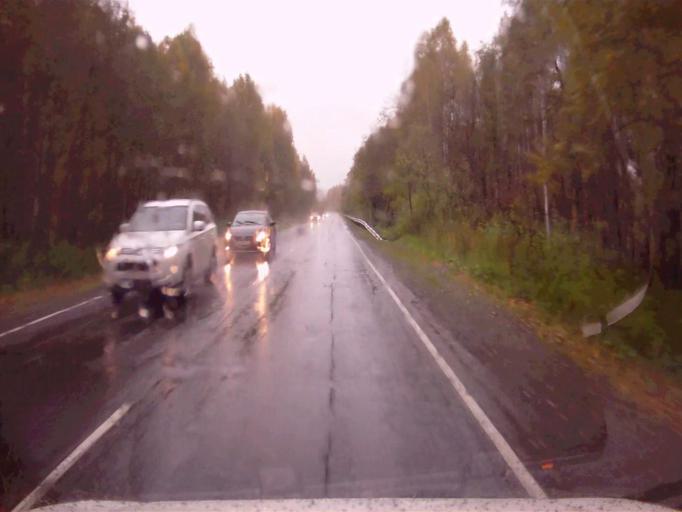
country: RU
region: Chelyabinsk
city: Verkhniy Ufaley
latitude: 55.9396
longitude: 60.4110
